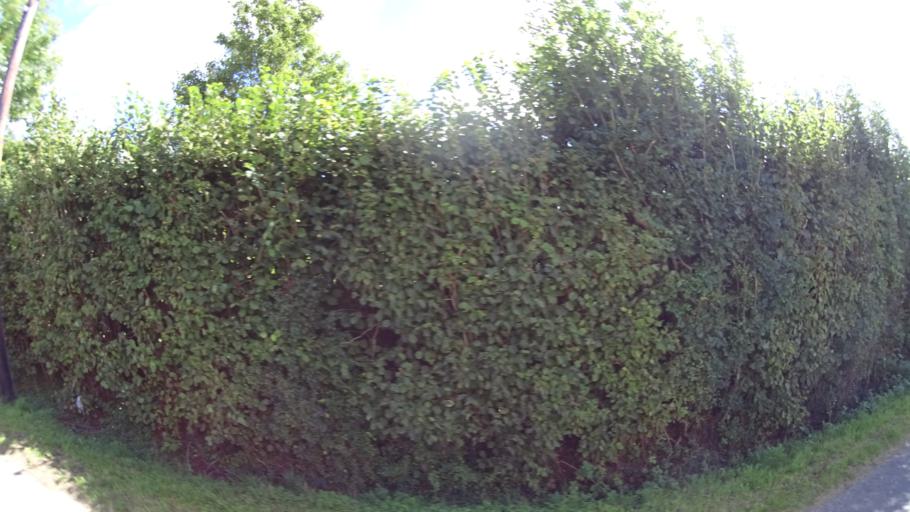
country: GB
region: England
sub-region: Hampshire
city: Romsey
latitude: 51.0156
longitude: -1.4697
